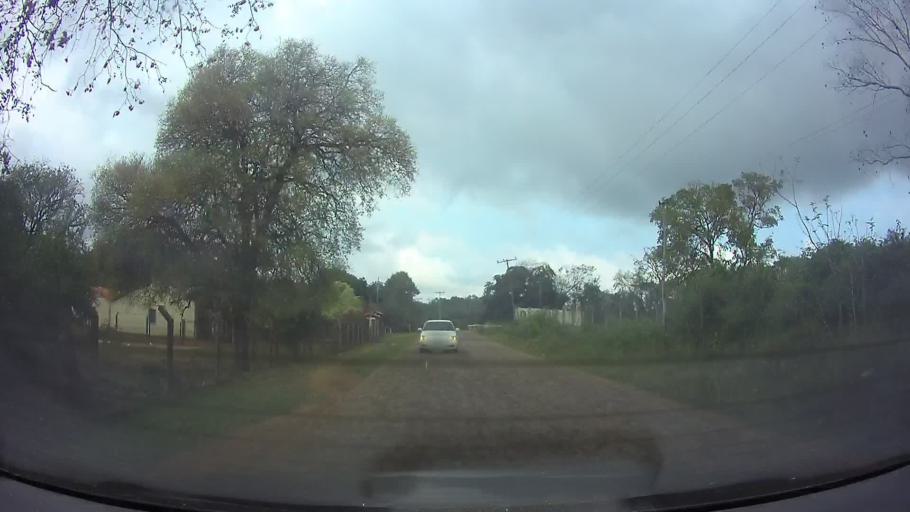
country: PY
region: Cordillera
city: Arroyos y Esteros
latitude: -25.0031
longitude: -57.1360
